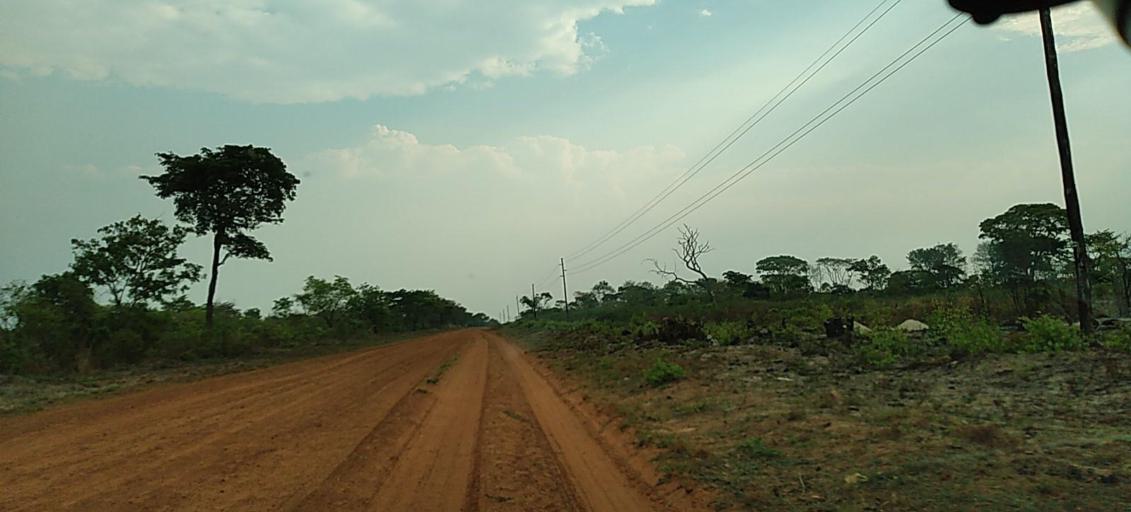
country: ZM
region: North-Western
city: Kabompo
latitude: -13.8963
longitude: 23.6575
